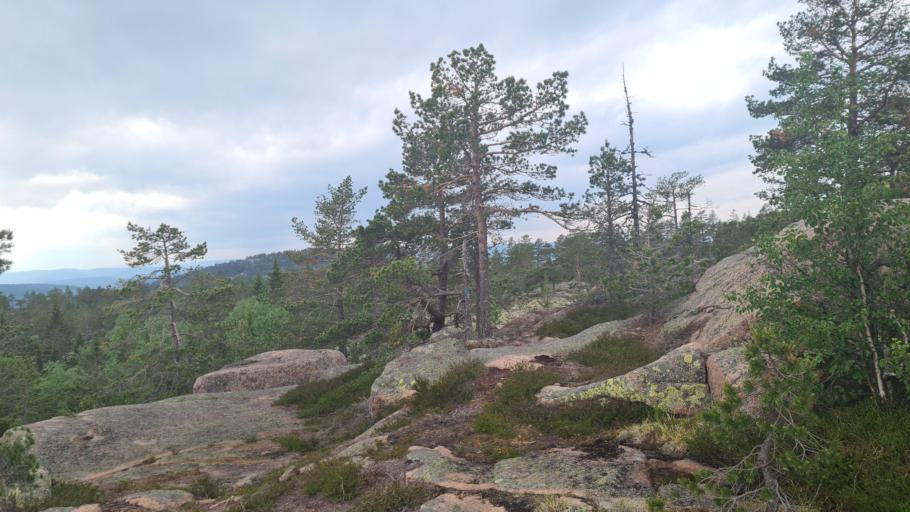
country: SE
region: Vaesternorrland
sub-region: Kramfors Kommun
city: Nordingra
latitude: 62.9836
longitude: 18.3922
